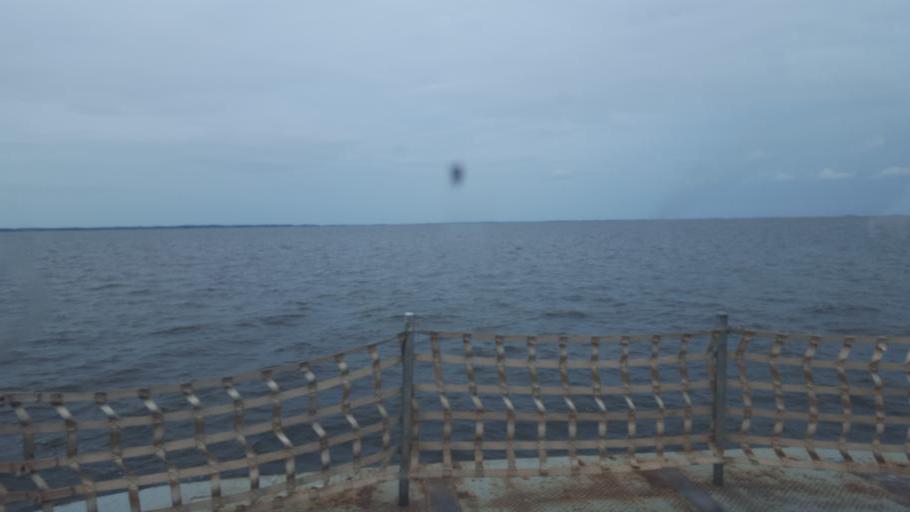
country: US
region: North Carolina
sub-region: Currituck County
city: Currituck
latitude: 36.4521
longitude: -76.0013
